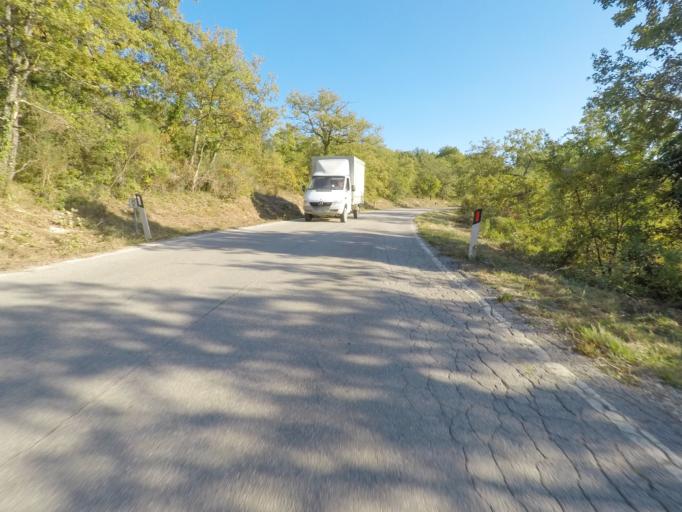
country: IT
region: Tuscany
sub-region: Provincia di Siena
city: Radda in Chianti
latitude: 43.4539
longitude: 11.3858
